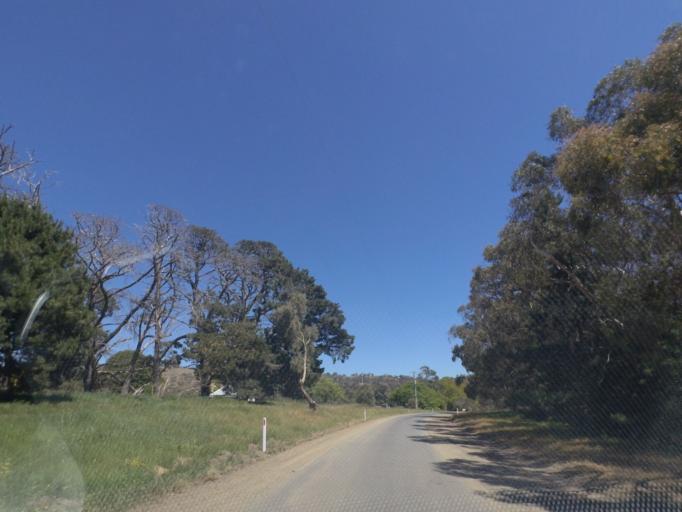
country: AU
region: Victoria
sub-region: Whittlesea
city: Whittlesea
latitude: -37.2903
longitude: 144.9873
